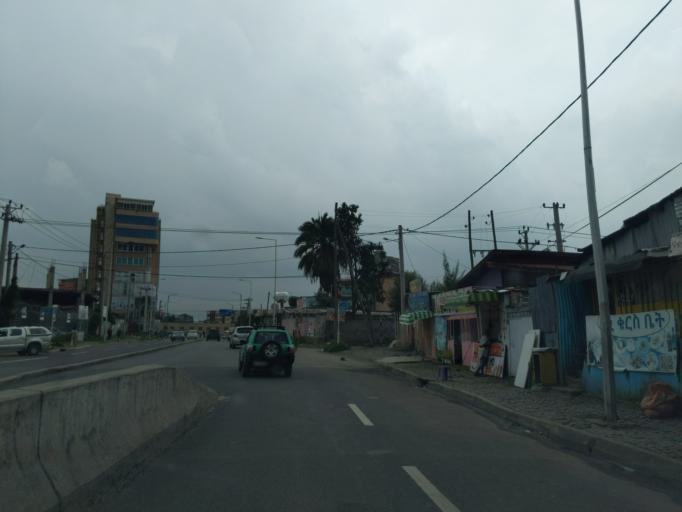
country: ET
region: Adis Abeba
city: Addis Ababa
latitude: 8.9857
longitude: 38.7654
